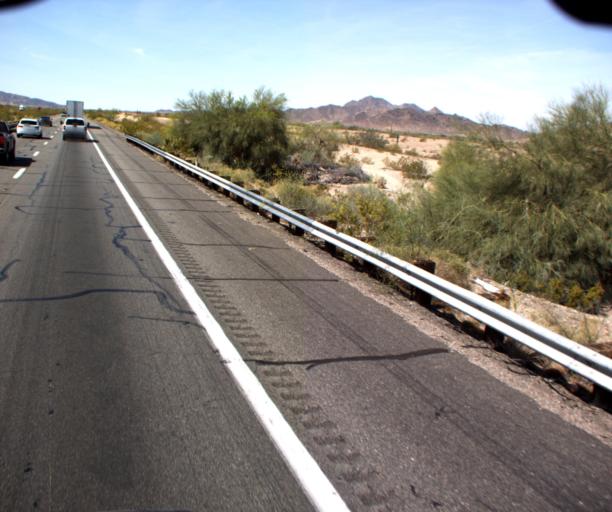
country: US
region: Arizona
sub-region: La Paz County
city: Quartzsite
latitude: 33.6570
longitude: -114.2612
